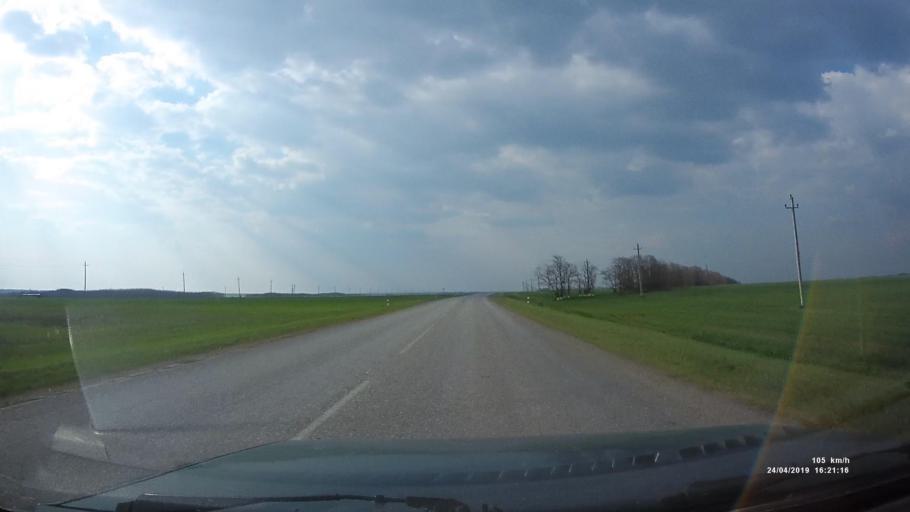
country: RU
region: Rostov
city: Orlovskiy
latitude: 46.8024
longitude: 42.0672
